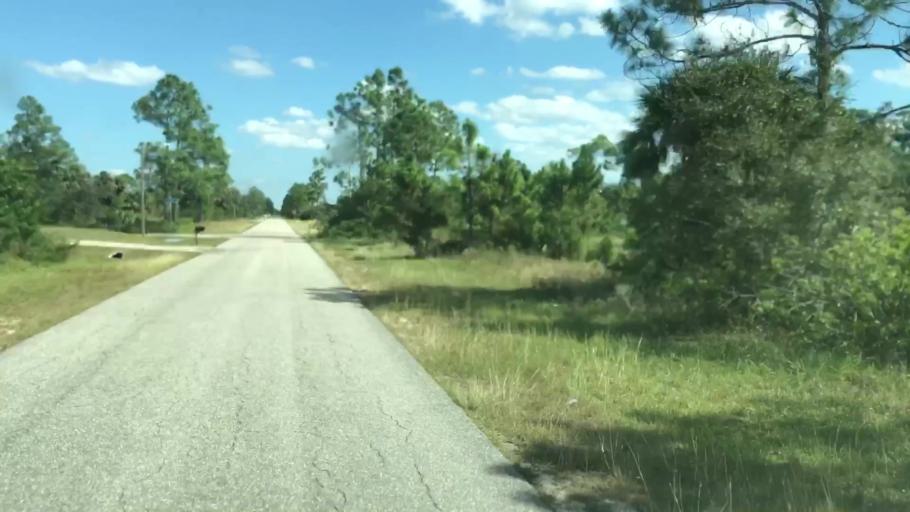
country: US
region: Florida
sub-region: Lee County
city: Lehigh Acres
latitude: 26.6285
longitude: -81.6272
